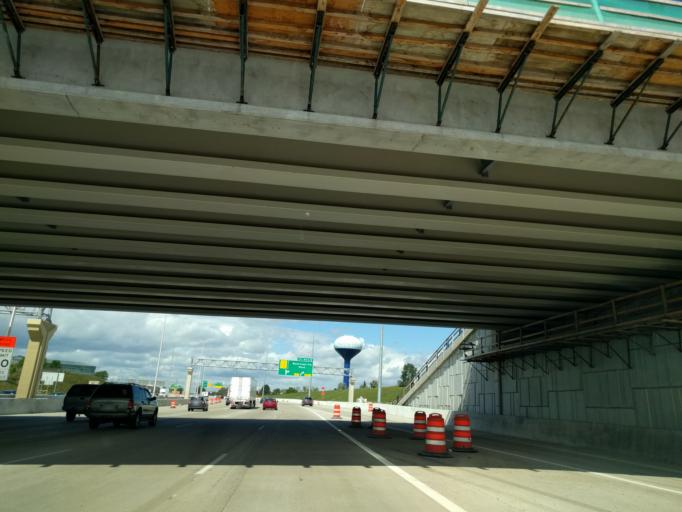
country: US
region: Wisconsin
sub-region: Milwaukee County
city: Wauwatosa
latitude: 43.0380
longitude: -88.0328
